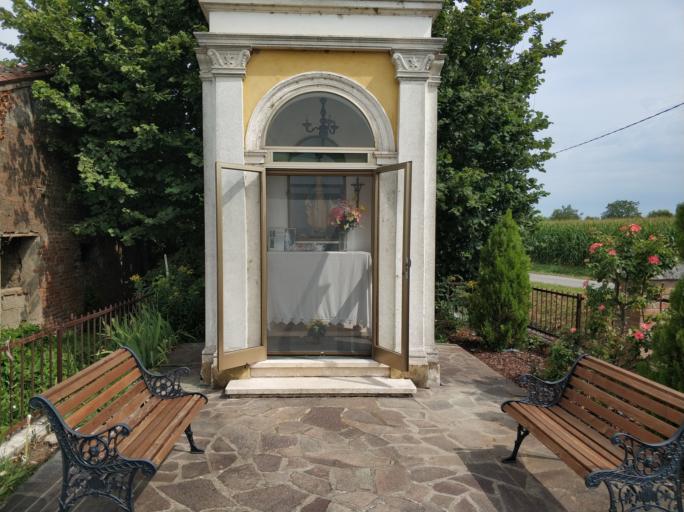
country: IT
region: Veneto
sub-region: Provincia di Padova
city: Megliadino San Fidenzio
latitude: 45.2372
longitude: 11.5059
